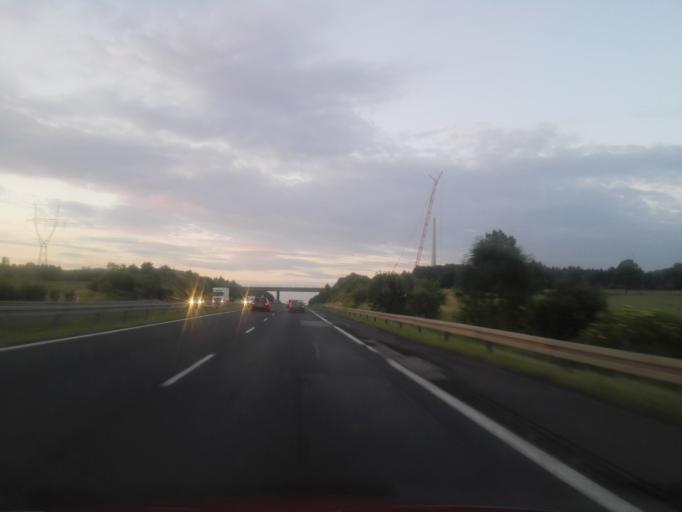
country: PL
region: Lodz Voivodeship
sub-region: Powiat radomszczanski
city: Radomsko
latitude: 51.1374
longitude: 19.4215
